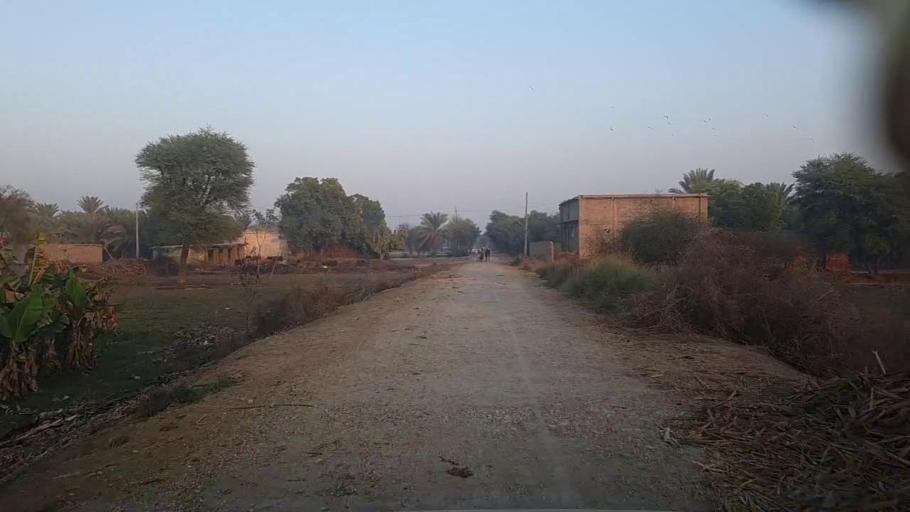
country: PK
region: Sindh
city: Karaundi
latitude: 26.8459
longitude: 68.3664
